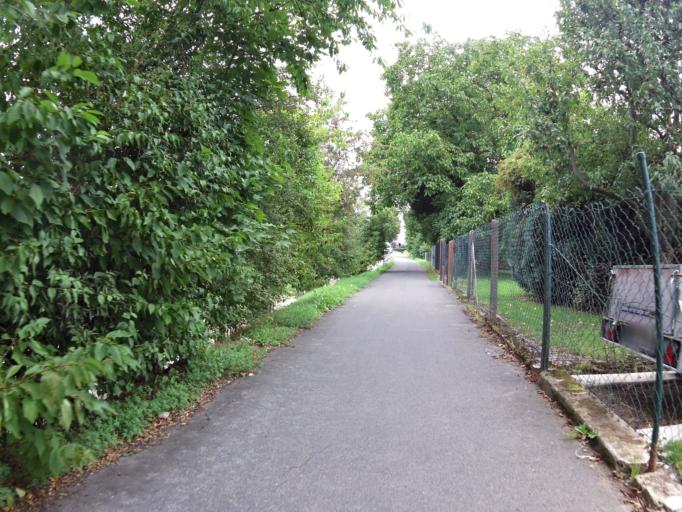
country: DE
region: Bavaria
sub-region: Upper Franconia
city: Viereth-Trunstadt
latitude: 49.9241
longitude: 10.7812
